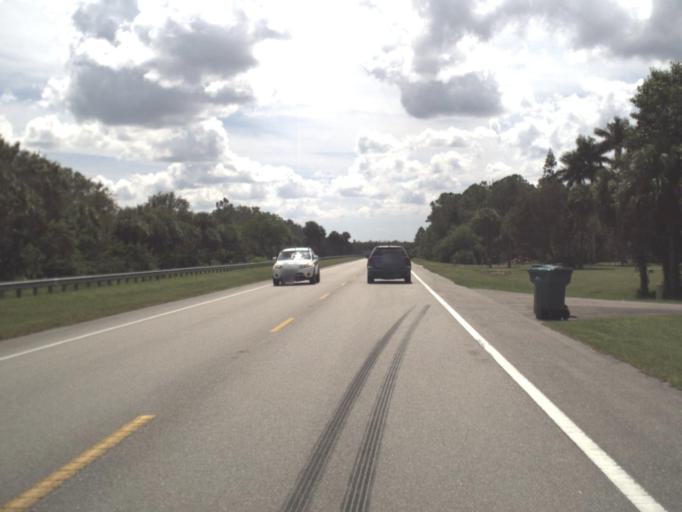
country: US
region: Florida
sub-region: Collier County
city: Lely Resort
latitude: 25.9944
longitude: -81.3473
